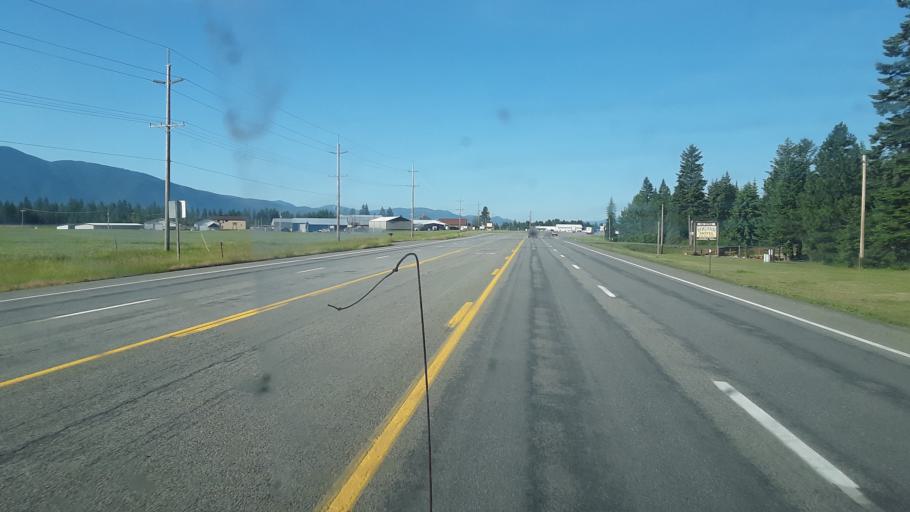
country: US
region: Idaho
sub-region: Boundary County
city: Bonners Ferry
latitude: 48.7276
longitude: -116.3017
